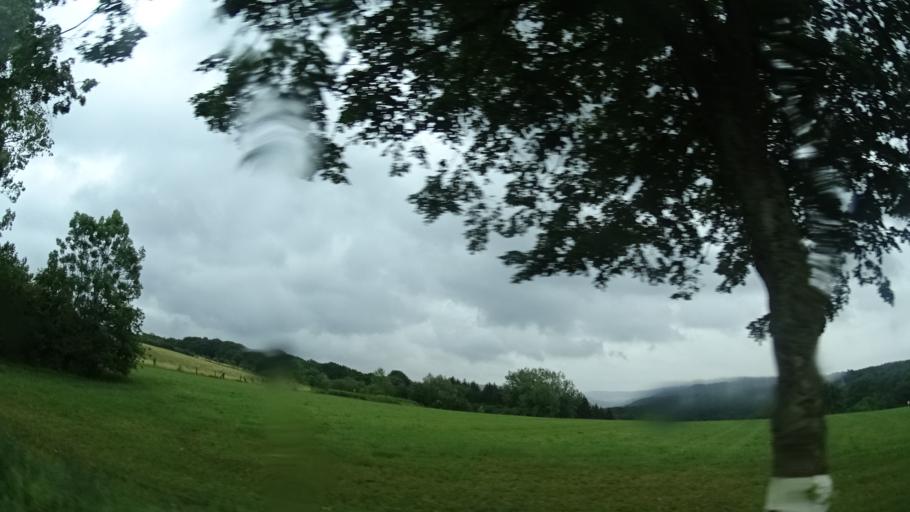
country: LU
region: Grevenmacher
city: Schengen
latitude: 49.4750
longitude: 6.3364
